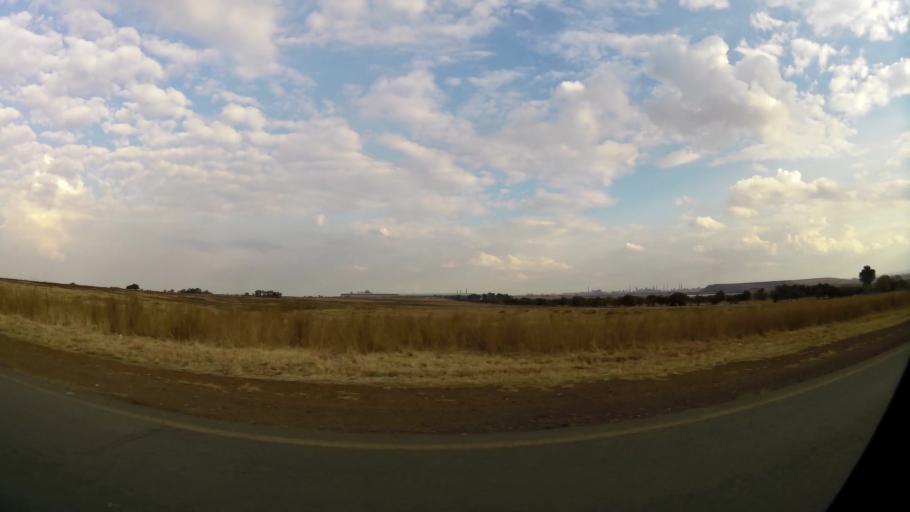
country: ZA
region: Gauteng
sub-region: Sedibeng District Municipality
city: Vanderbijlpark
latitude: -26.6186
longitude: 27.8373
